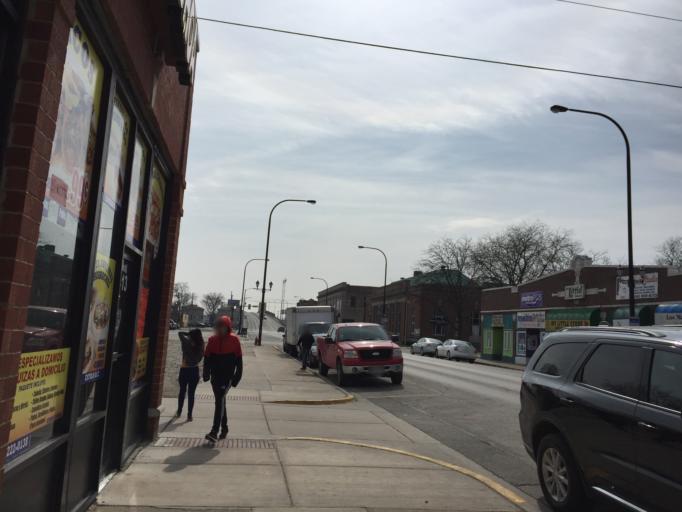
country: US
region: Illinois
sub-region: Cook County
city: Cicero
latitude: 41.8471
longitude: -87.7538
